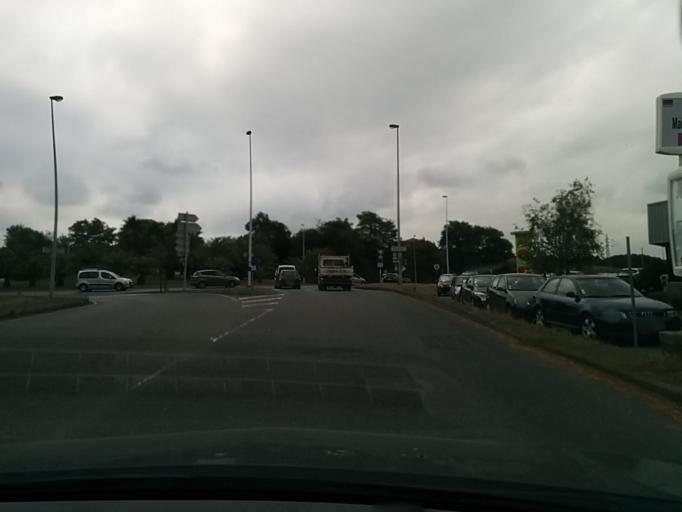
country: FR
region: Aquitaine
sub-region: Departement des Pyrenees-Atlantiques
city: Anglet
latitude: 43.4662
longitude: -1.4963
